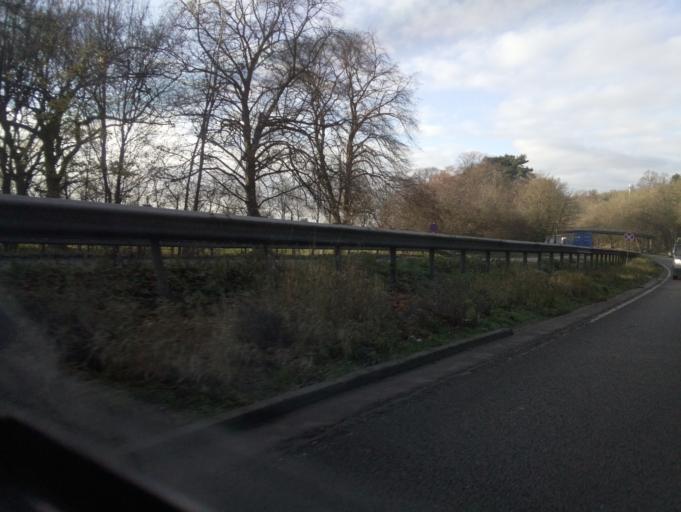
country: GB
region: England
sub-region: Staffordshire
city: Burton upon Trent
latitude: 52.8149
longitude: -1.6537
